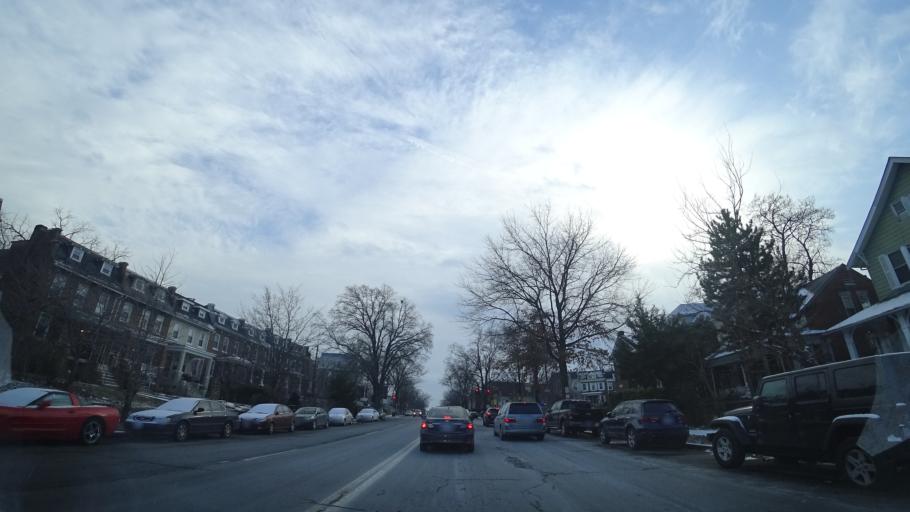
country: US
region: Maryland
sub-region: Montgomery County
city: Takoma Park
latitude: 38.9468
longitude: -77.0268
